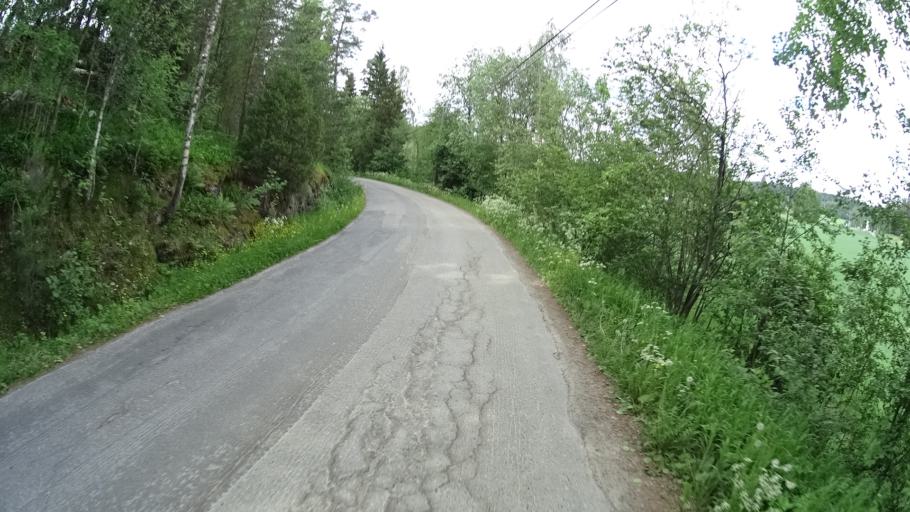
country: FI
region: Uusimaa
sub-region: Helsinki
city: Sibbo
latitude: 60.2897
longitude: 25.3101
